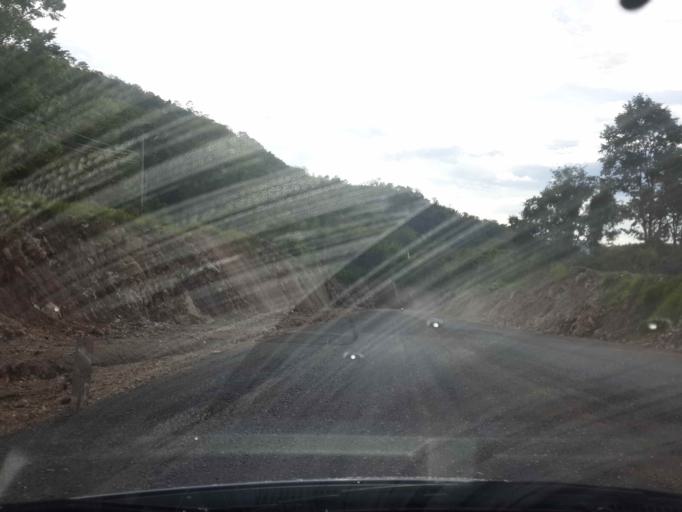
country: TH
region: Kanchanaburi
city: Sai Yok
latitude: 13.9305
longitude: 99.1041
